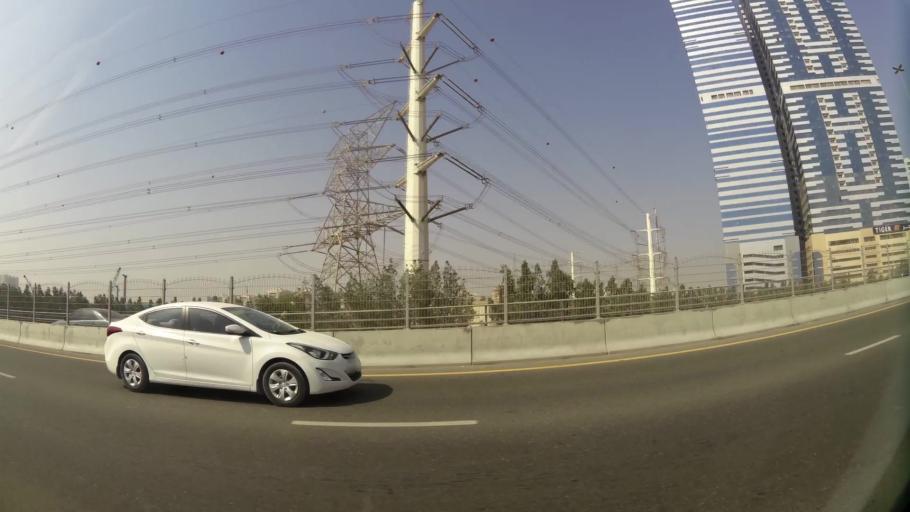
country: AE
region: Ash Shariqah
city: Sharjah
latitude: 25.3027
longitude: 55.3861
